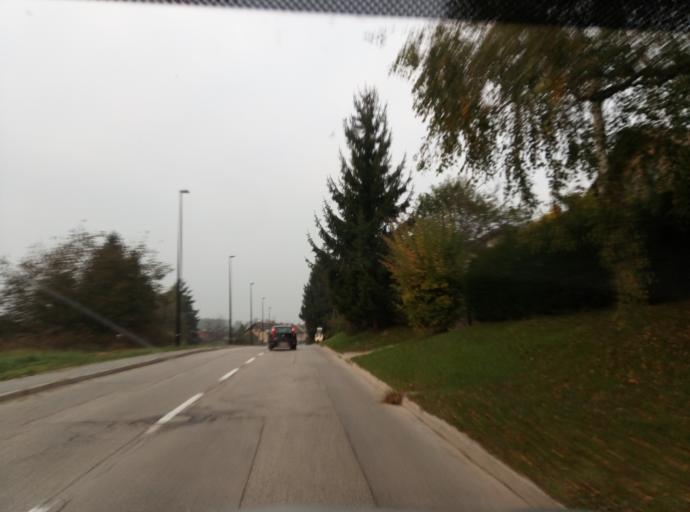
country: SI
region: Ljubljana
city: Ljubljana
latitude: 46.0880
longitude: 14.4668
